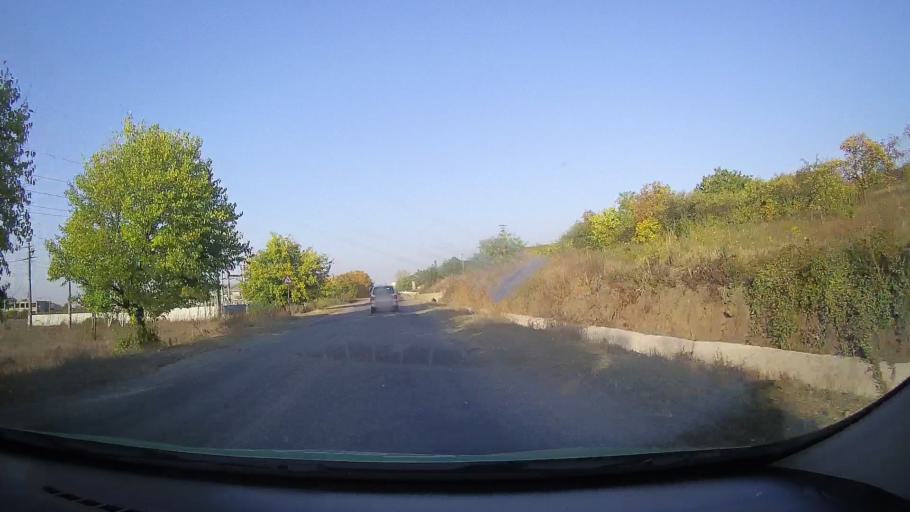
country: RO
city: Masca
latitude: 46.3155
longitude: 21.6804
